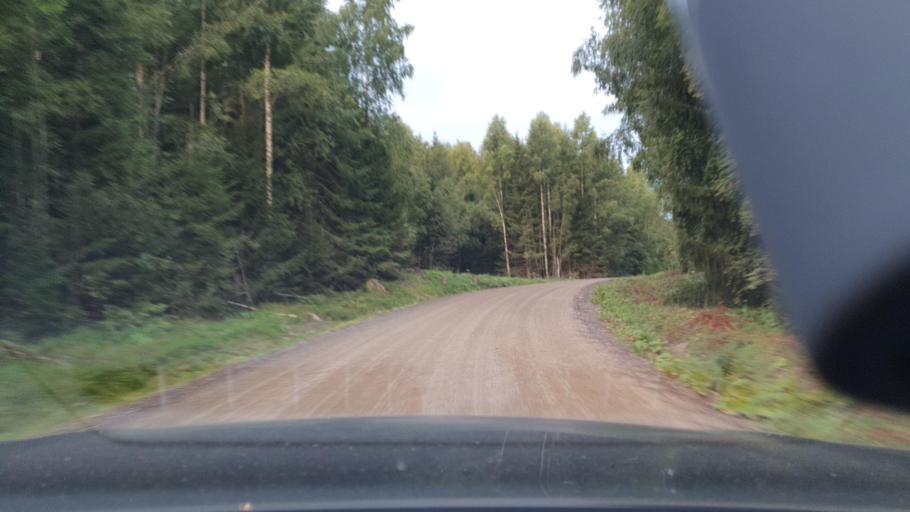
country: SE
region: Vaermland
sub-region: Sunne Kommun
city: Sunne
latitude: 59.8438
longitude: 12.9381
